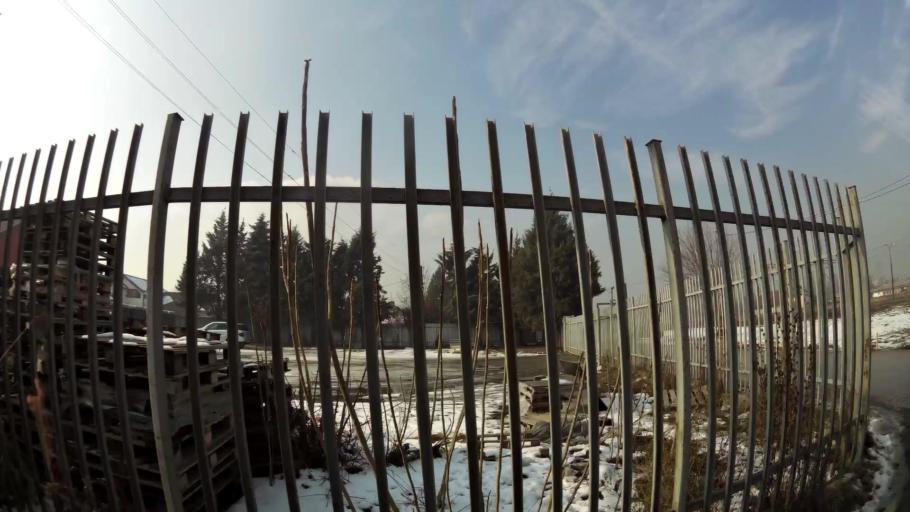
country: MK
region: Kisela Voda
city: Kisela Voda
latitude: 41.9929
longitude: 21.5014
